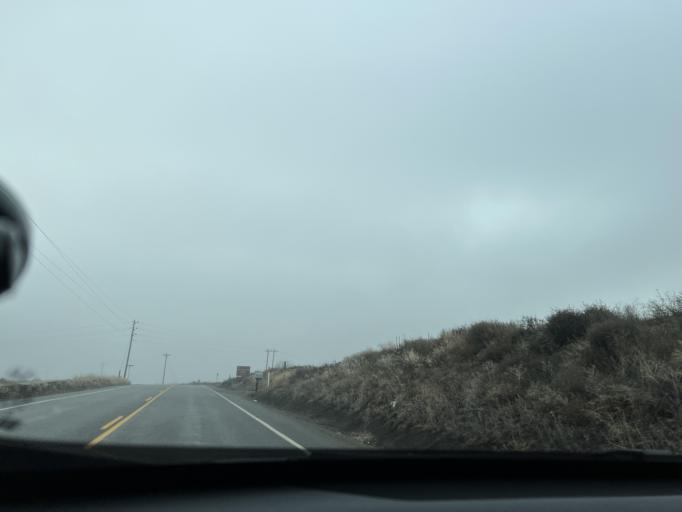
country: US
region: Washington
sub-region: Okanogan County
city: Brewster
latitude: 48.4469
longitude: -120.2015
